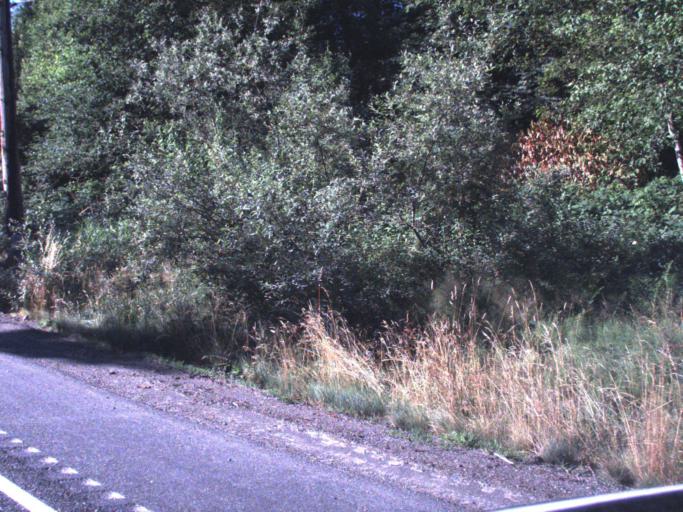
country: US
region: Washington
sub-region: King County
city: Enumclaw
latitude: 47.1787
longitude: -121.9196
